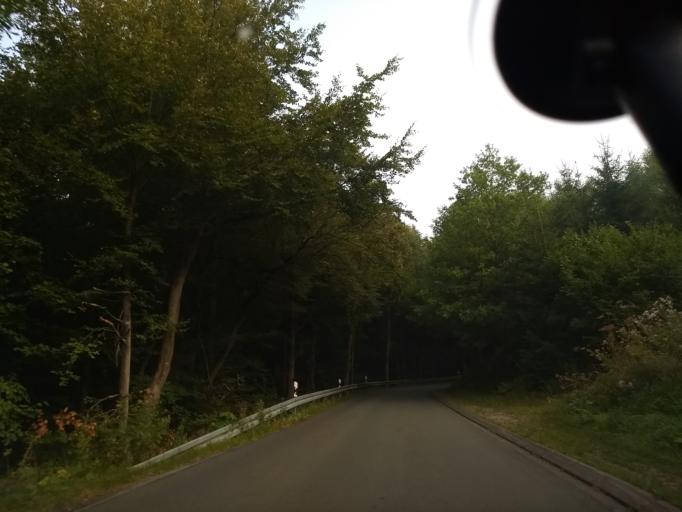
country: DE
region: North Rhine-Westphalia
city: Eslohe
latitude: 51.2514
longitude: 8.0863
